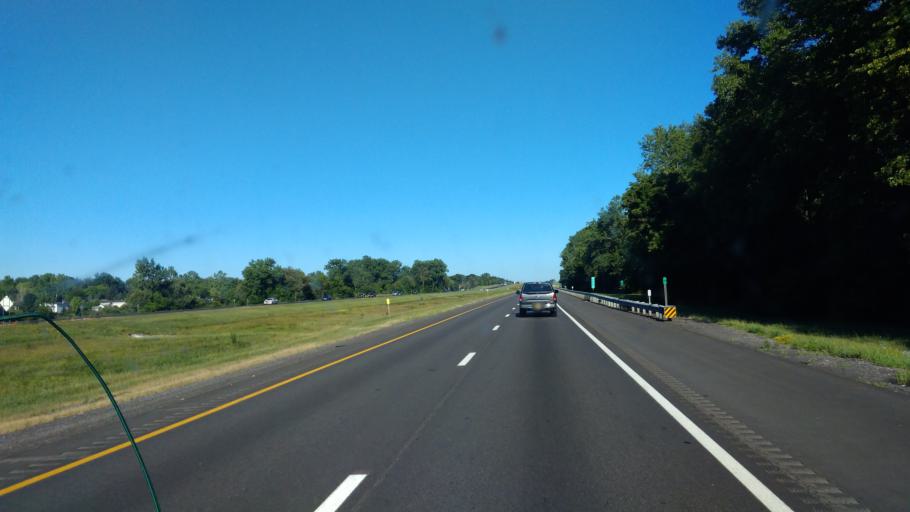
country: US
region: New York
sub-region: Ontario County
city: Clifton Springs
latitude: 42.9734
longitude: -77.1505
